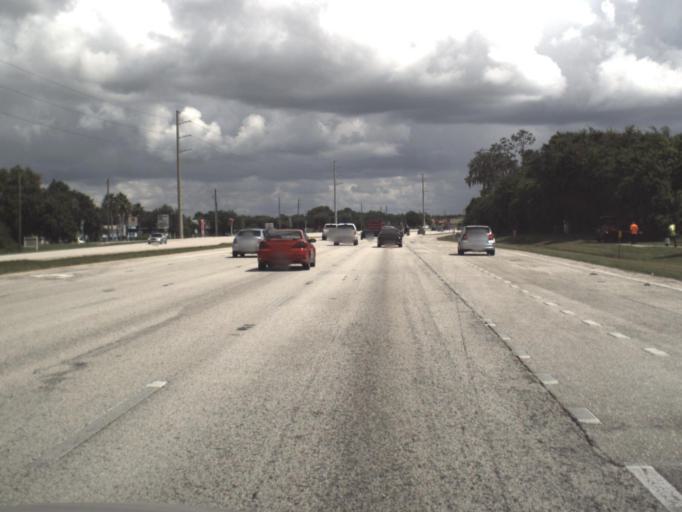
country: US
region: Florida
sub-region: Manatee County
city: Samoset
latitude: 27.4459
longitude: -82.4777
